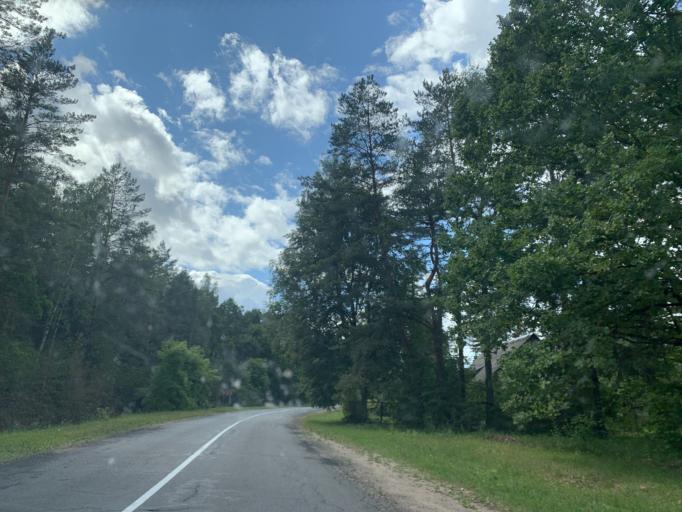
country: BY
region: Minsk
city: Rakaw
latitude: 53.9860
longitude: 26.9527
